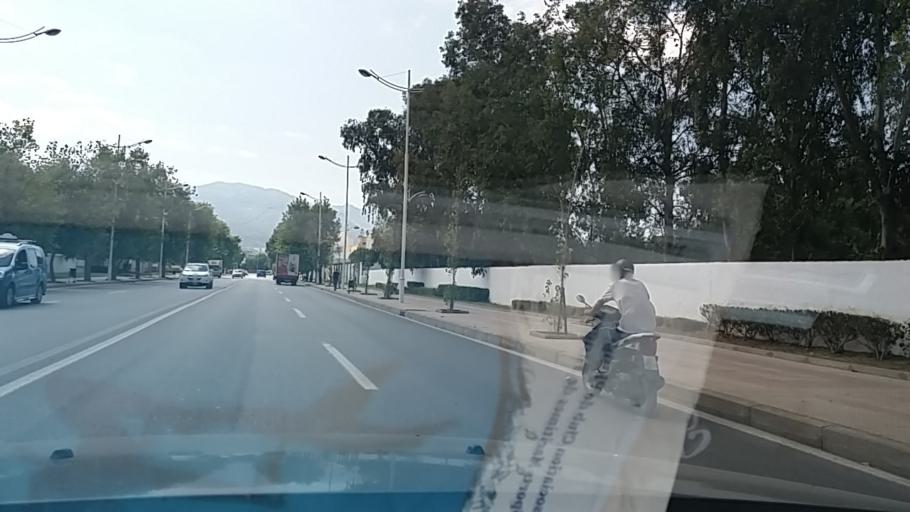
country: MA
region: Tanger-Tetouan
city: Tetouan
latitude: 35.5789
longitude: -5.3387
